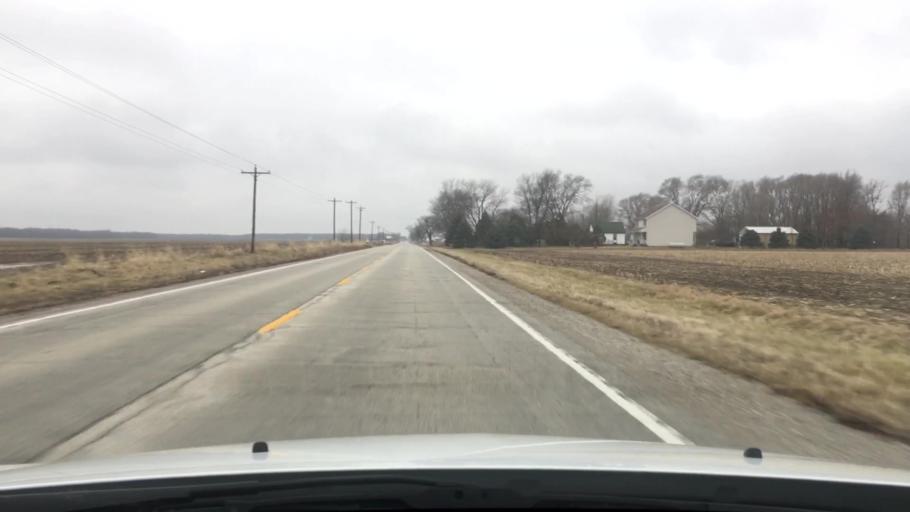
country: US
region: Illinois
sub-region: Iroquois County
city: Watseka
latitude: 40.8887
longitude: -87.7918
